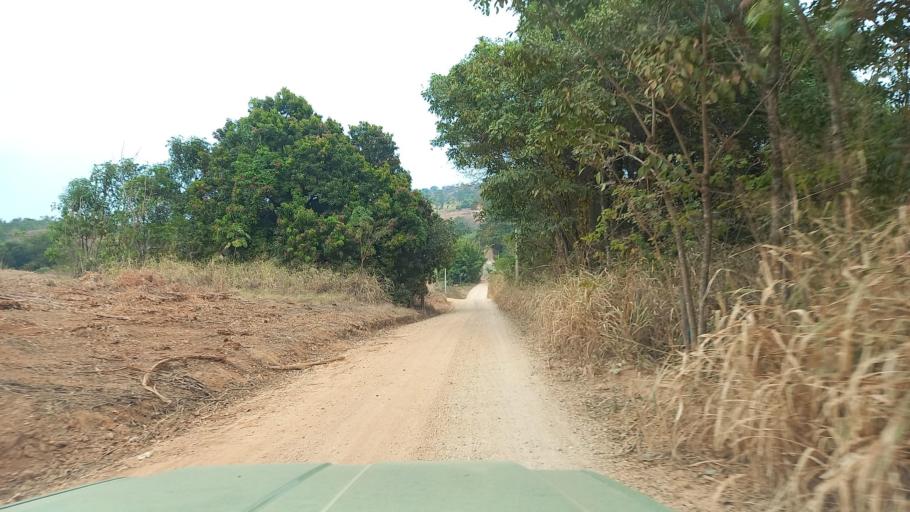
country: BR
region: Sao Paulo
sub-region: Moji-Guacu
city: Mogi-Gaucu
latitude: -22.2813
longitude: -46.8453
